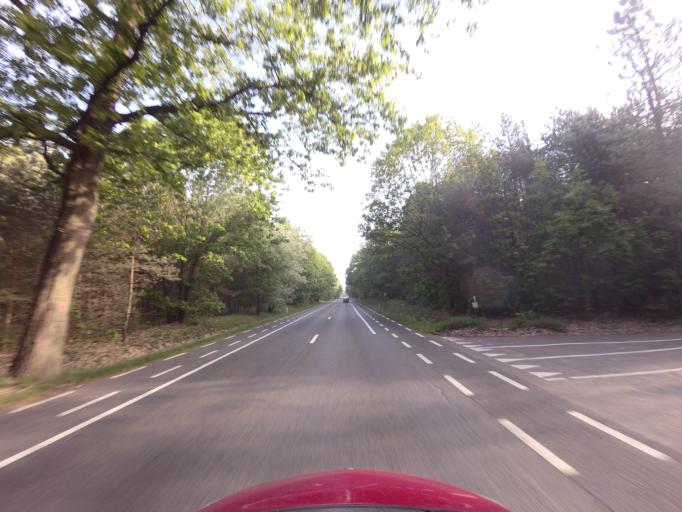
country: BE
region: Flanders
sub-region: Provincie Limburg
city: Overpelt
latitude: 51.2096
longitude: 5.3627
